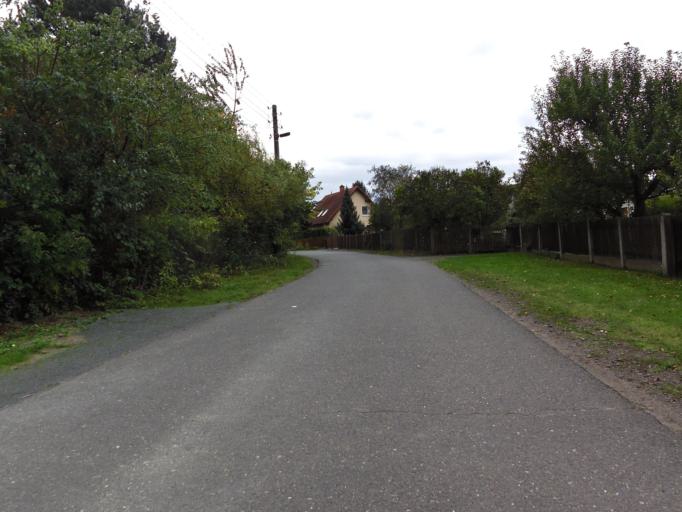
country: DE
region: Saxony
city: Grossposna
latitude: 51.3143
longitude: 12.4701
